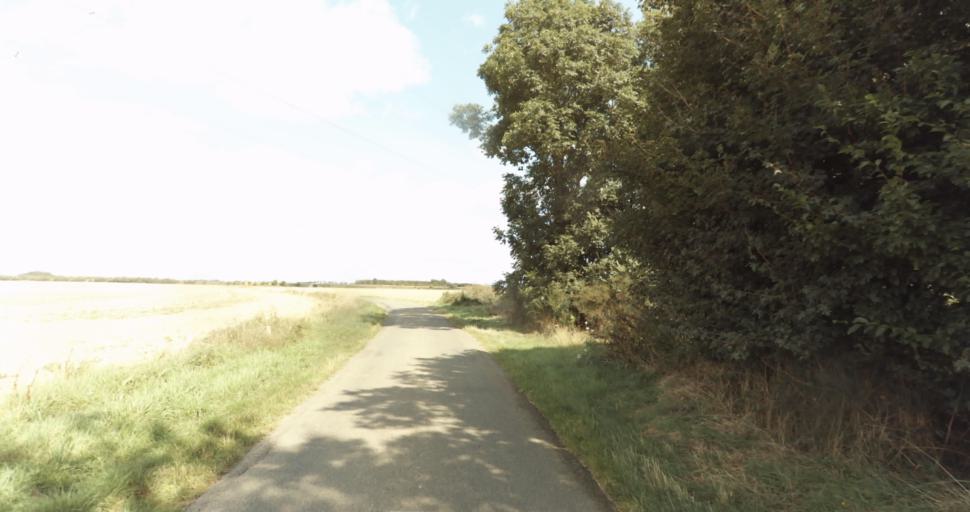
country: FR
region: Haute-Normandie
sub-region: Departement de l'Eure
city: La Madeleine-de-Nonancourt
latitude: 48.8575
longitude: 1.1683
